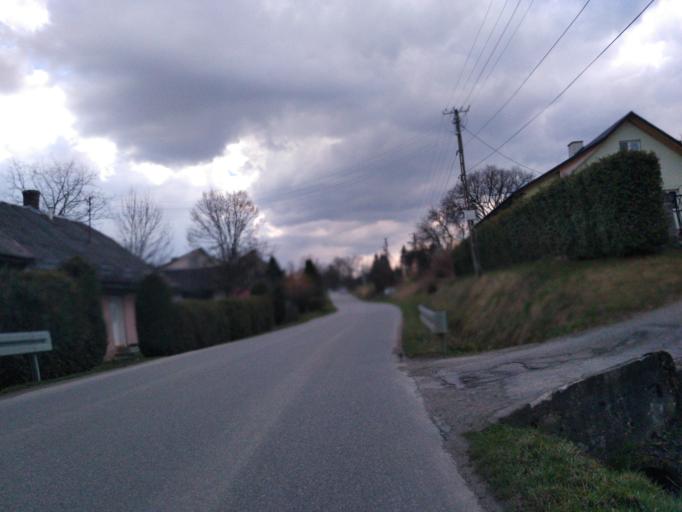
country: PL
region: Subcarpathian Voivodeship
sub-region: Powiat brzozowski
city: Dydnia
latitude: 49.6750
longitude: 22.1854
